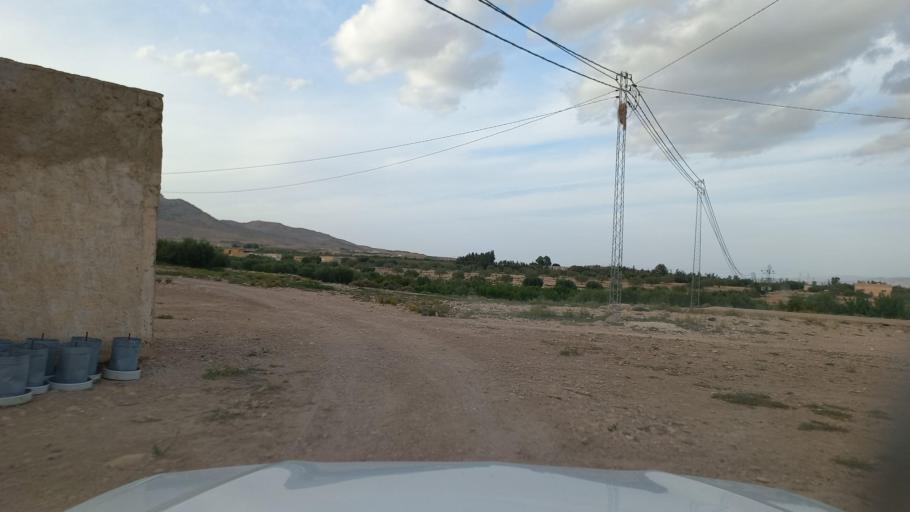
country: TN
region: Al Qasrayn
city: Sbiba
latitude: 35.4369
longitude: 9.0944
